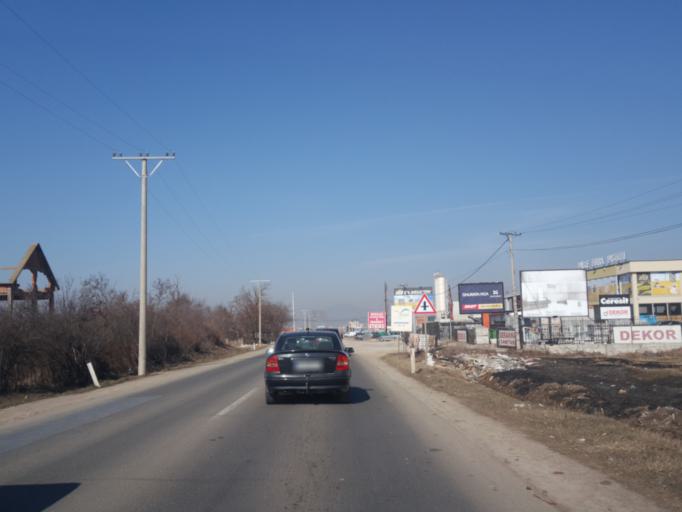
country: XK
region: Mitrovica
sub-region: Vushtrri
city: Vushtrri
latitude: 42.7982
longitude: 20.9975
